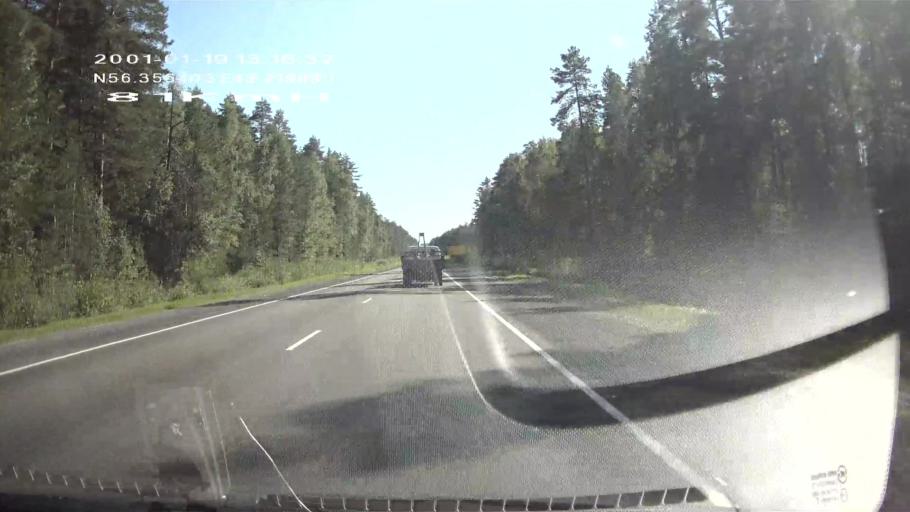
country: RU
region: Mariy-El
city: Suslonger
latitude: 56.3562
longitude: 48.2201
